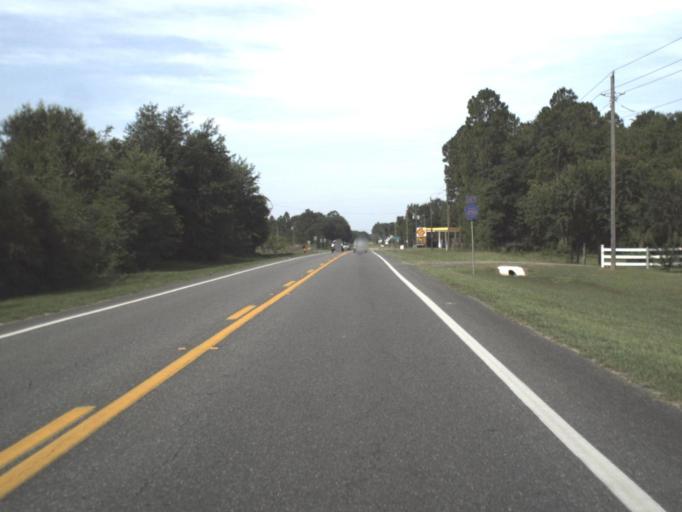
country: US
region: Florida
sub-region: Suwannee County
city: Live Oak
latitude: 30.2482
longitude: -83.0449
